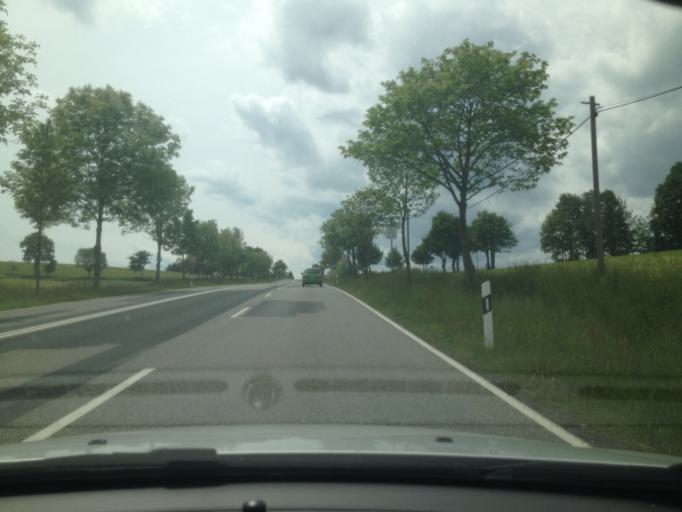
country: DE
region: Saxony
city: Lossnitz
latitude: 50.6633
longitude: 12.7580
